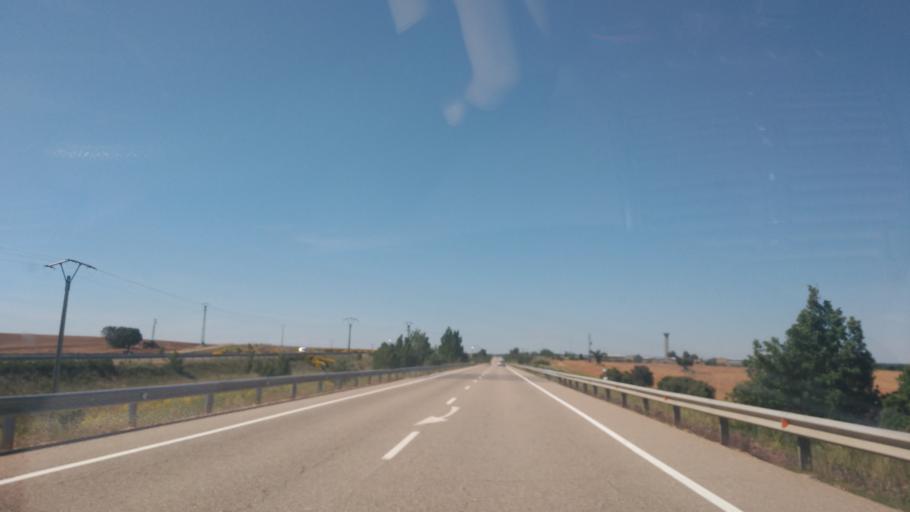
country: ES
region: Castille and Leon
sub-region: Provincia de Salamanca
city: Topas
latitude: 41.1845
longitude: -5.6951
